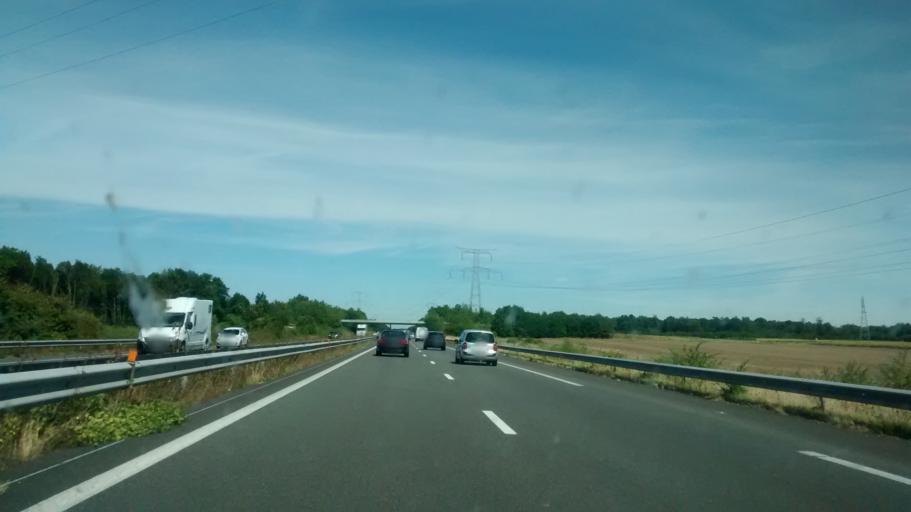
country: FR
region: Poitou-Charentes
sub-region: Departement de la Charente-Maritime
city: Saint-Genis-de-Saintonge
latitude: 45.5336
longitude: -0.6080
